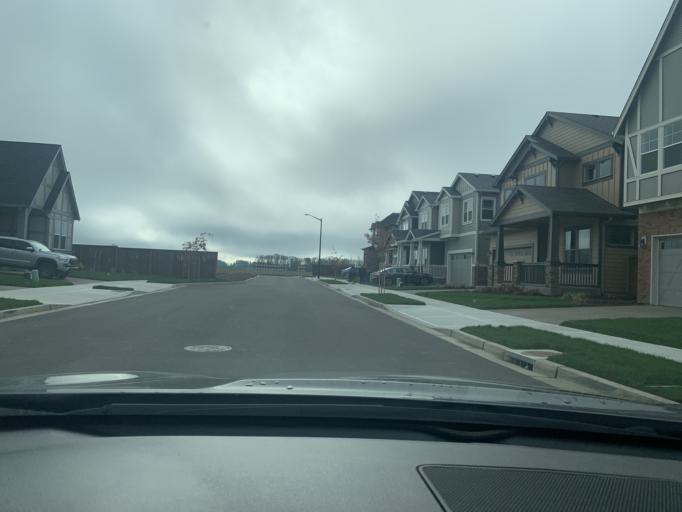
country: US
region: Oregon
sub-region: Washington County
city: North Plains
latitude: 45.5933
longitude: -122.9744
